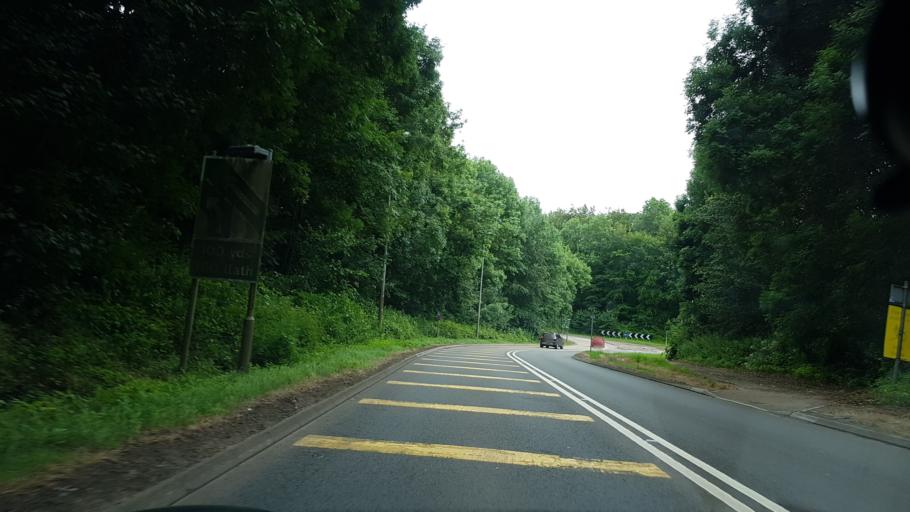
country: GB
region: Wales
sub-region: Monmouthshire
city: Abergavenny
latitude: 51.8104
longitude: -3.0072
